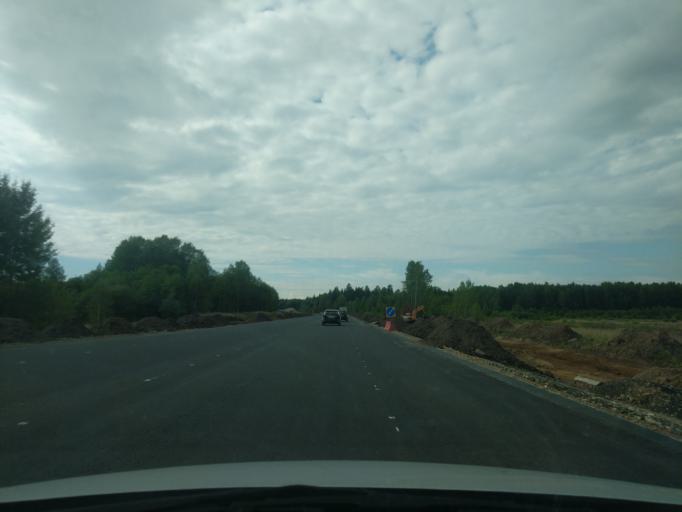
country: RU
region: Kostroma
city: Sudislavl'
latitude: 57.8272
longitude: 41.5247
